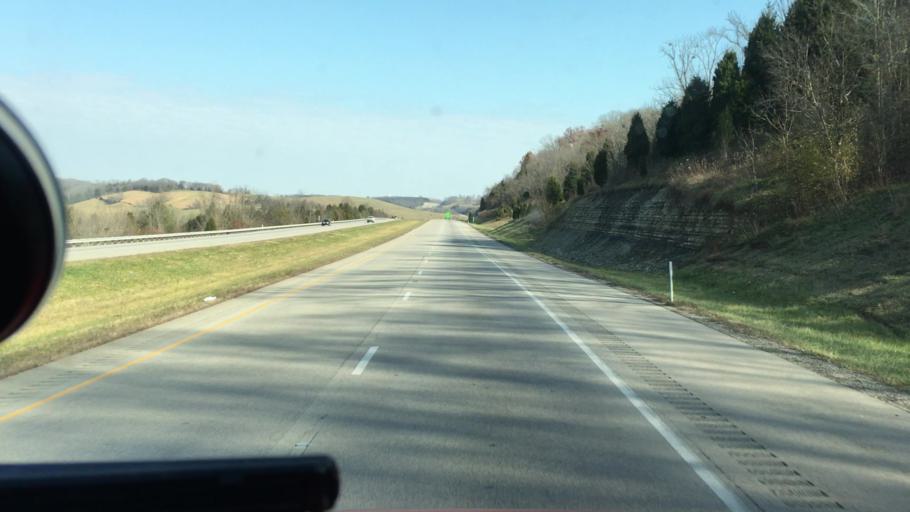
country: US
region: Kentucky
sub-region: Bath County
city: Owingsville
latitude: 38.1065
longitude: -83.8223
